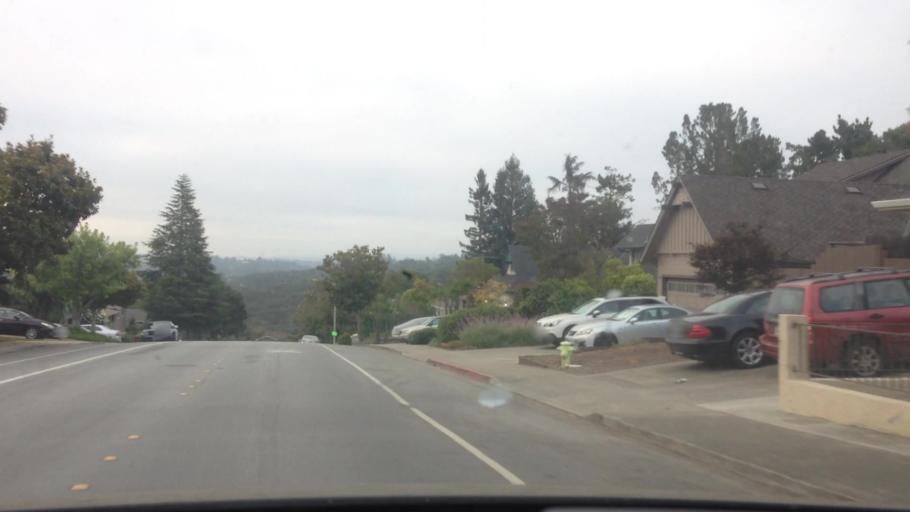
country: US
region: California
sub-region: San Mateo County
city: Emerald Lake Hills
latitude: 37.4569
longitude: -122.2548
